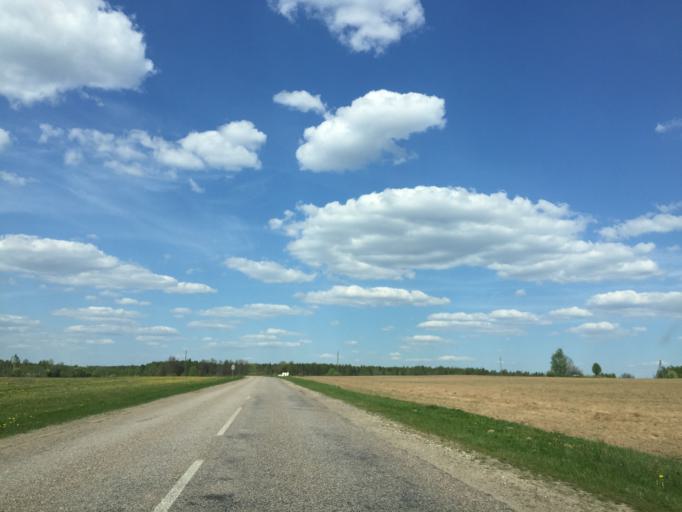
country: LV
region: Limbazu Rajons
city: Limbazi
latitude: 57.3835
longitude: 24.6862
